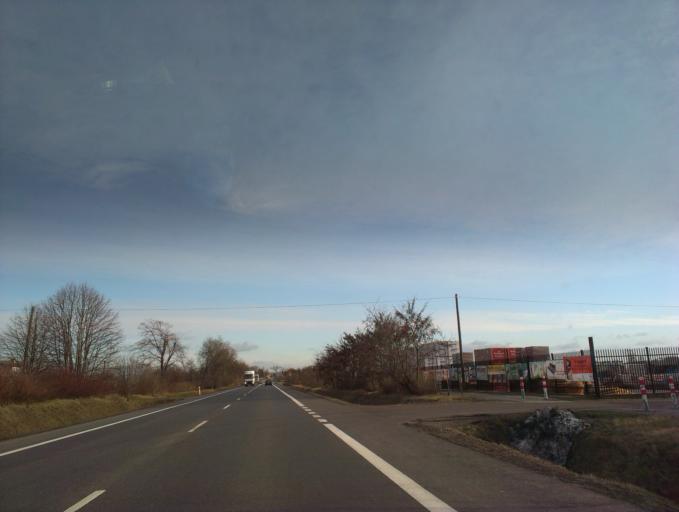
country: PL
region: Kujawsko-Pomorskie
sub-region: Powiat torunski
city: Obrowo
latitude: 52.9696
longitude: 18.8929
